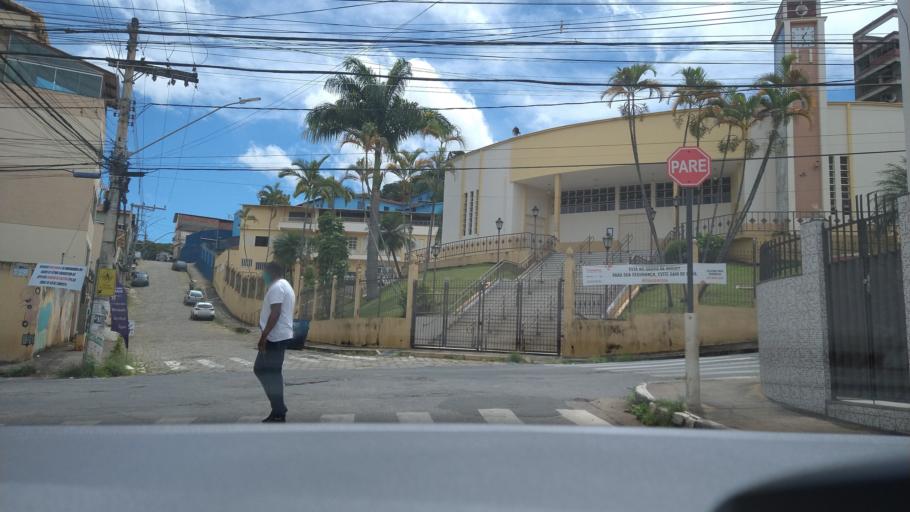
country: BR
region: Minas Gerais
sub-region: Vicosa
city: Vicosa
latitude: -20.7648
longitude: -42.8857
